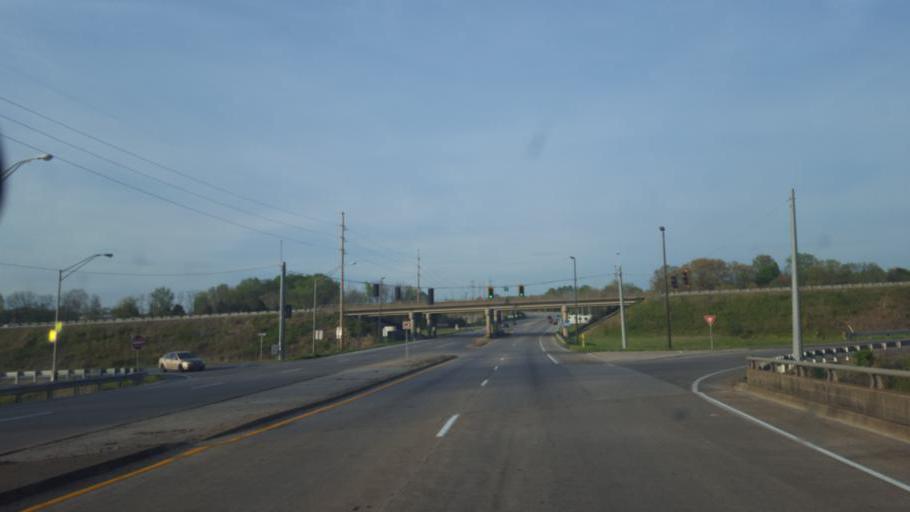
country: US
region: Kentucky
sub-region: Barren County
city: Glasgow
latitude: 36.9769
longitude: -85.9358
